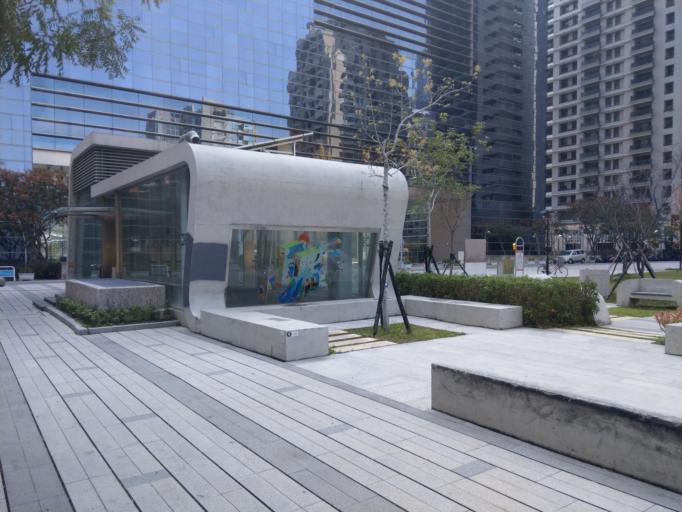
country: TW
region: Taiwan
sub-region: Taichung City
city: Taichung
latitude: 24.1590
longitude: 120.6455
